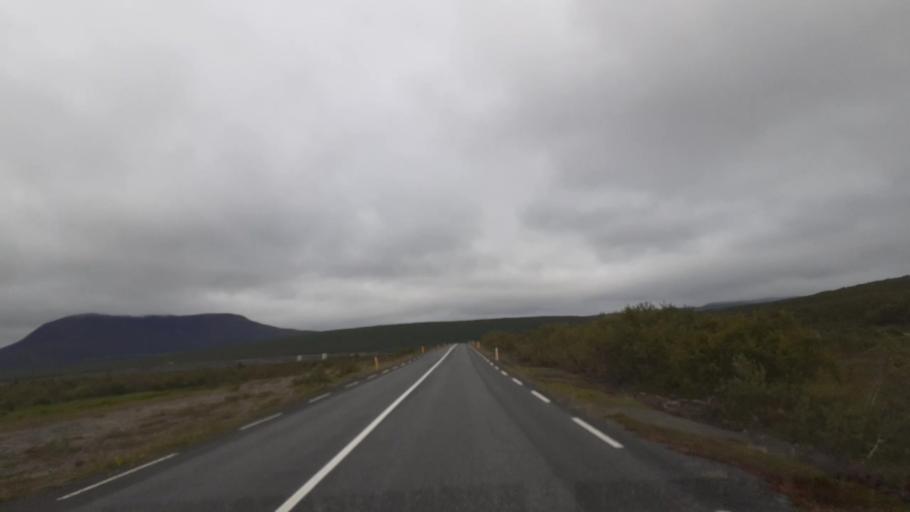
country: IS
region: Northeast
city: Husavik
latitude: 66.0308
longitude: -16.4758
